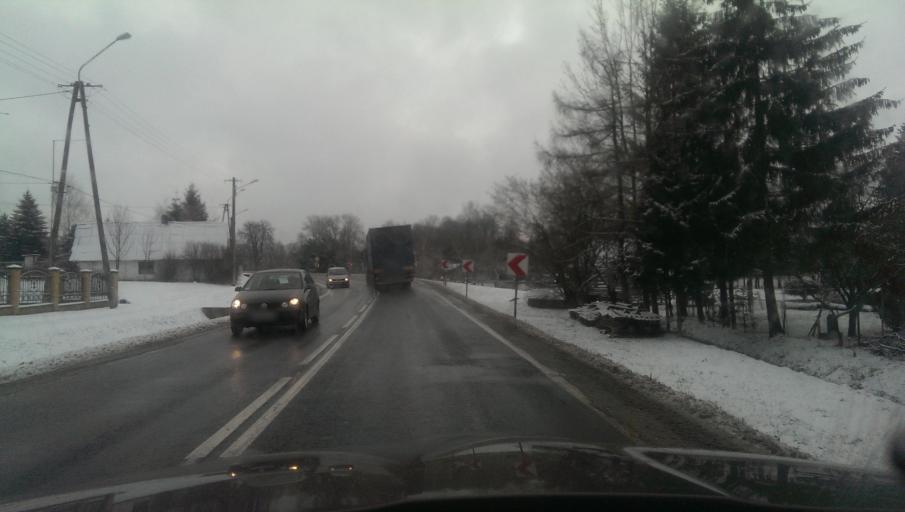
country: PL
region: Subcarpathian Voivodeship
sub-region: Powiat sanocki
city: Nowosielce-Gniewosz
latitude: 49.5590
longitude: 22.0940
